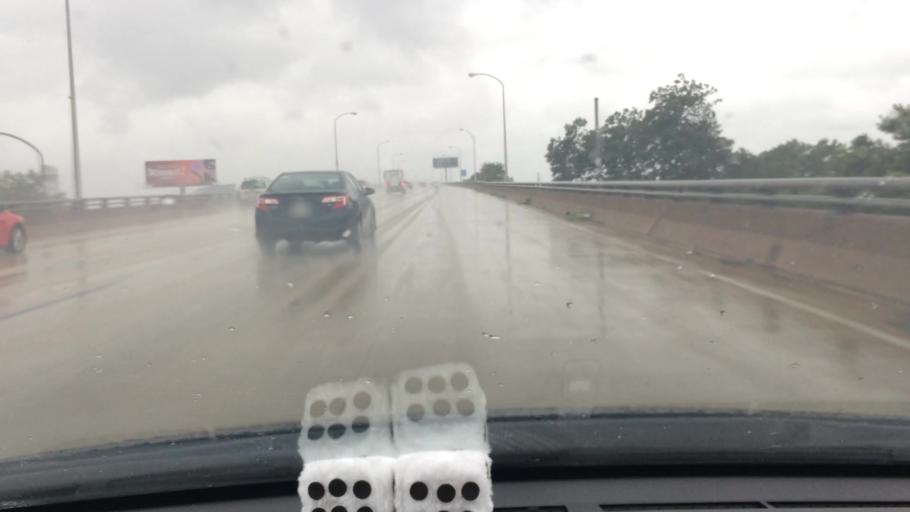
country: US
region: New Jersey
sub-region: Gloucester County
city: National Park
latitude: 39.8988
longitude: -75.1829
